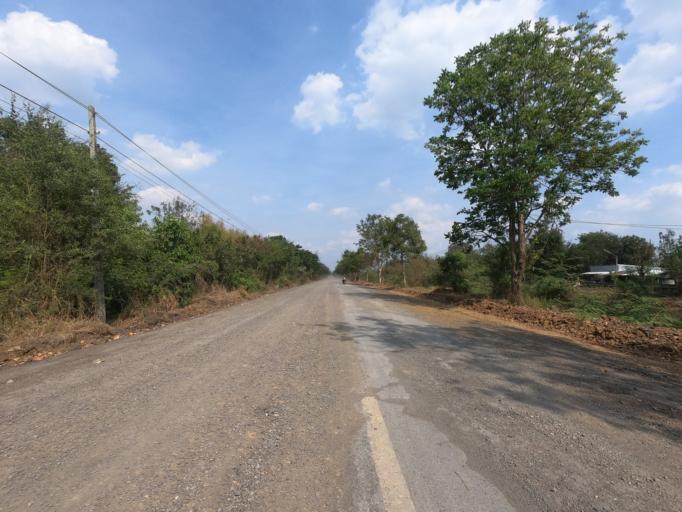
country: TH
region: Sara Buri
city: Nong Khae
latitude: 14.2560
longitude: 100.8490
